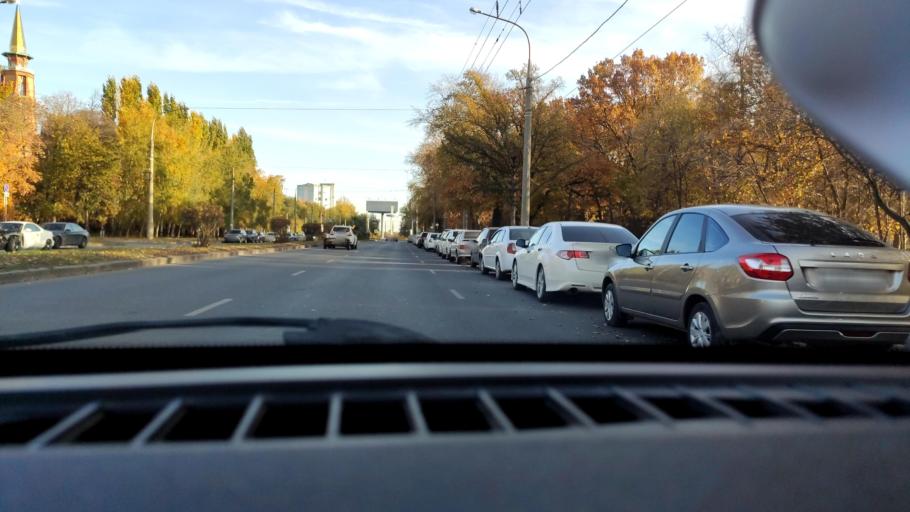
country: RU
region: Samara
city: Samara
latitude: 53.2308
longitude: 50.2043
